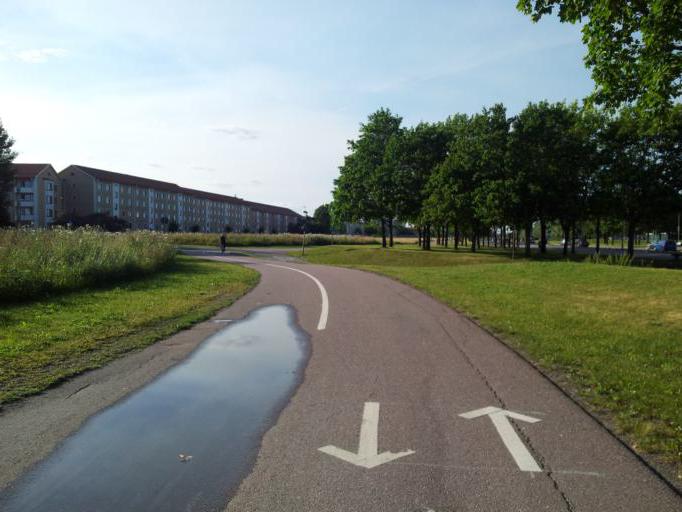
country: SE
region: Uppsala
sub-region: Uppsala Kommun
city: Uppsala
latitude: 59.8646
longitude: 17.6818
